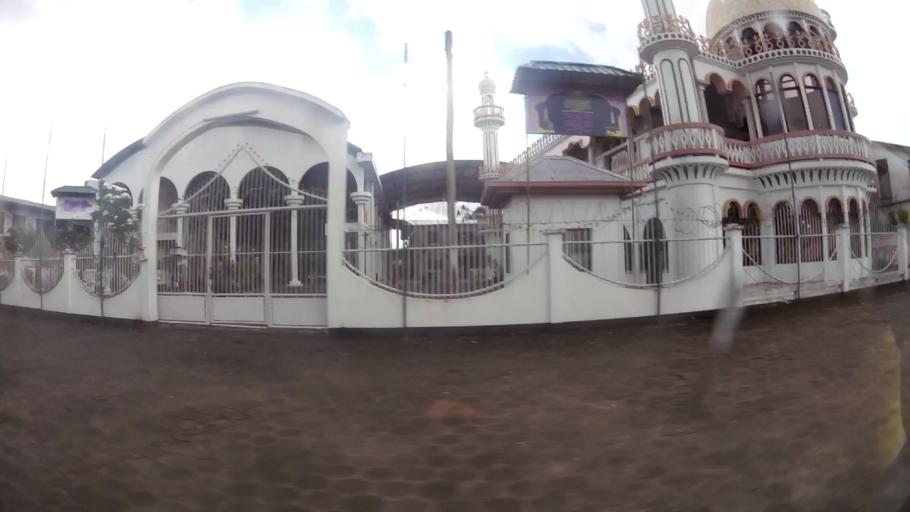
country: SR
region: Paramaribo
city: Paramaribo
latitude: 5.8336
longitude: -55.1453
